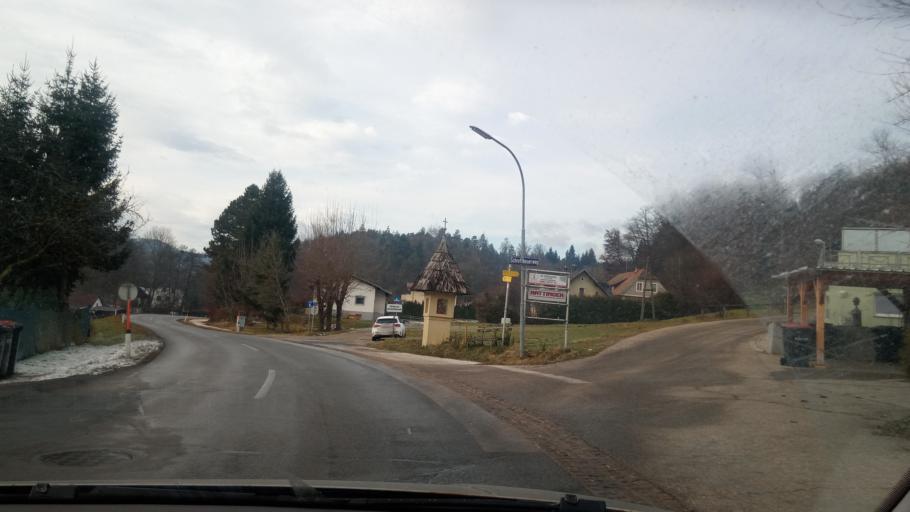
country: AT
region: Carinthia
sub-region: Politischer Bezirk Klagenfurt Land
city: Kottmannsdorf
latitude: 46.5903
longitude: 14.2553
